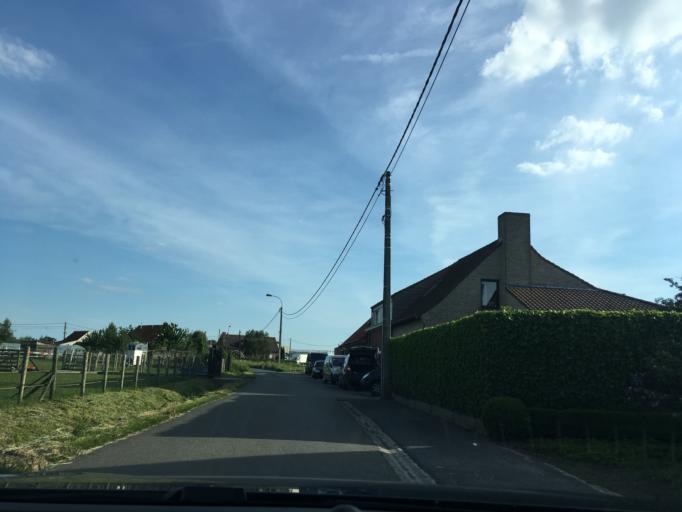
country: BE
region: Flanders
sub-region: Provincie West-Vlaanderen
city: Hooglede
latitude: 50.9476
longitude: 3.0702
